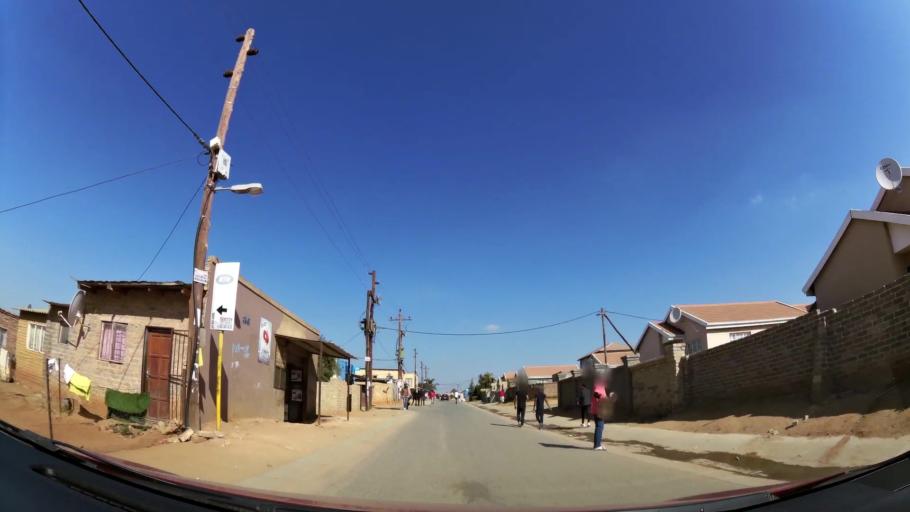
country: ZA
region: Gauteng
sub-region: West Rand District Municipality
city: Muldersdriseloop
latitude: -26.0260
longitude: 27.9281
